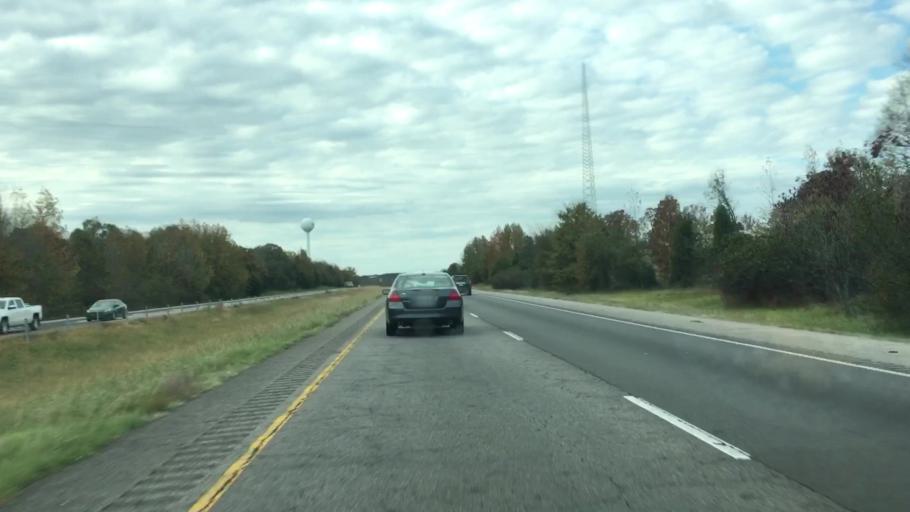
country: US
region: Arkansas
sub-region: Faulkner County
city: Conway
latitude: 35.1459
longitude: -92.5366
